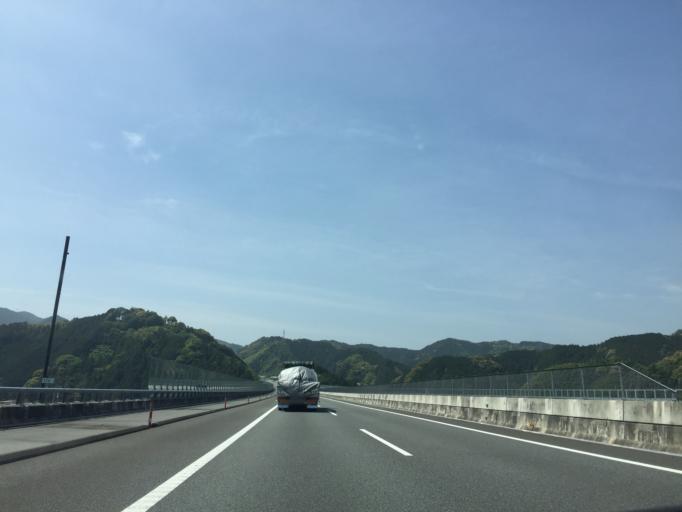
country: JP
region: Shizuoka
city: Shizuoka-shi
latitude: 34.9912
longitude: 138.2994
